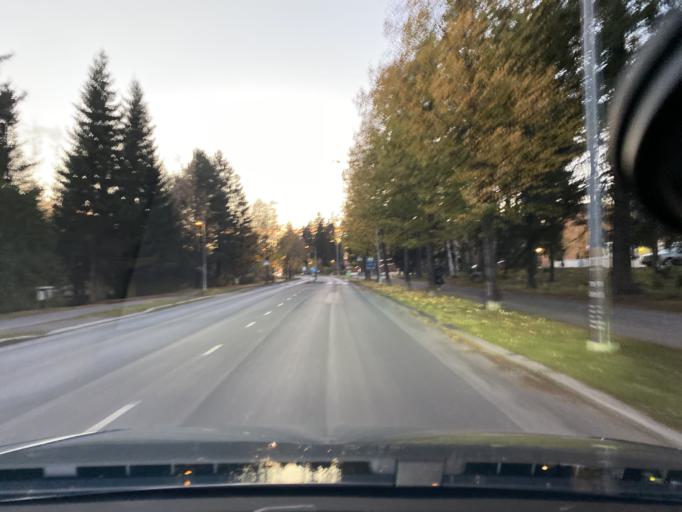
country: FI
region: Pirkanmaa
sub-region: Tampere
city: Tampere
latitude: 61.4701
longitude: 23.7464
